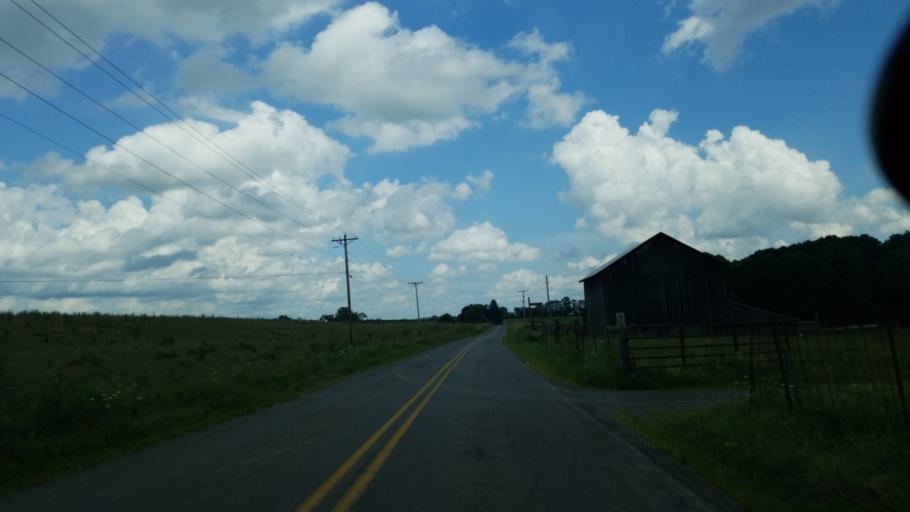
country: US
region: Pennsylvania
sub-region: Jefferson County
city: Brookville
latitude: 41.2390
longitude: -79.0381
